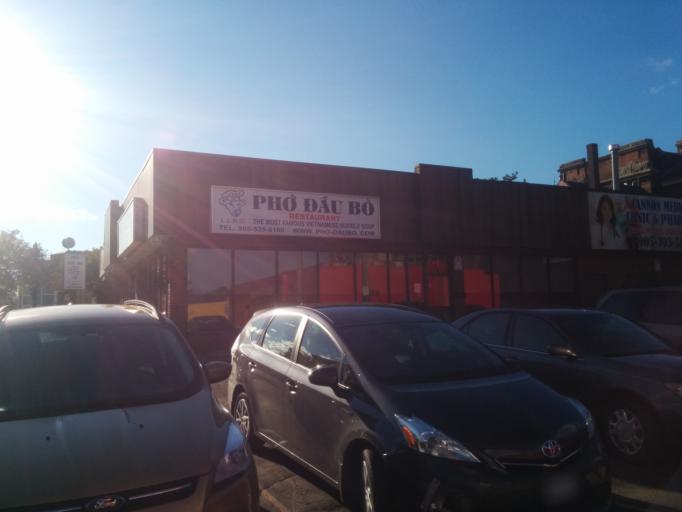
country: CA
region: Ontario
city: Hamilton
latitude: 43.2608
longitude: -79.8666
